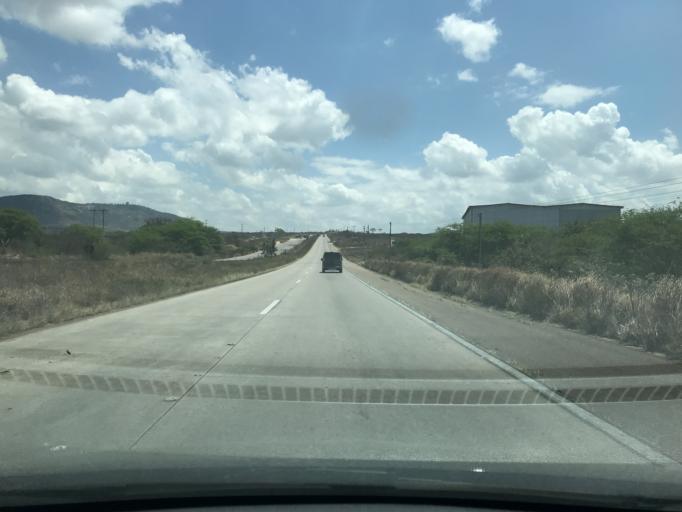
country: BR
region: Pernambuco
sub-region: Bezerros
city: Bezerros
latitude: -8.2902
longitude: -35.8218
